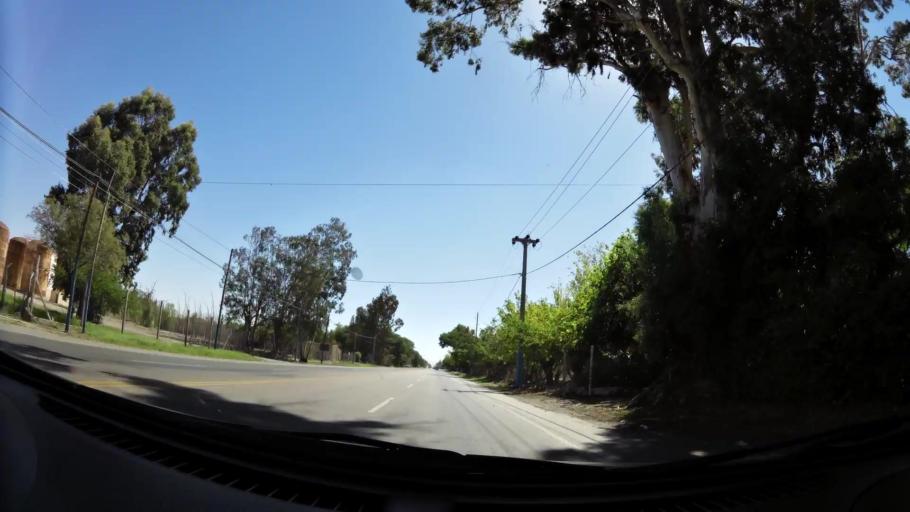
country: AR
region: San Juan
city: Villa Aberastain
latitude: -31.6165
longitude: -68.5486
